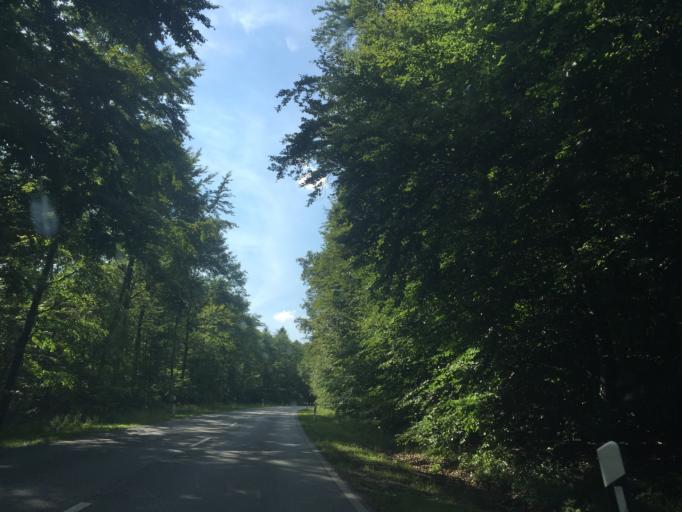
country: DE
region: Baden-Wuerttemberg
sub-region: Karlsruhe Region
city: Gaiberg
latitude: 49.3711
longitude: 8.7350
